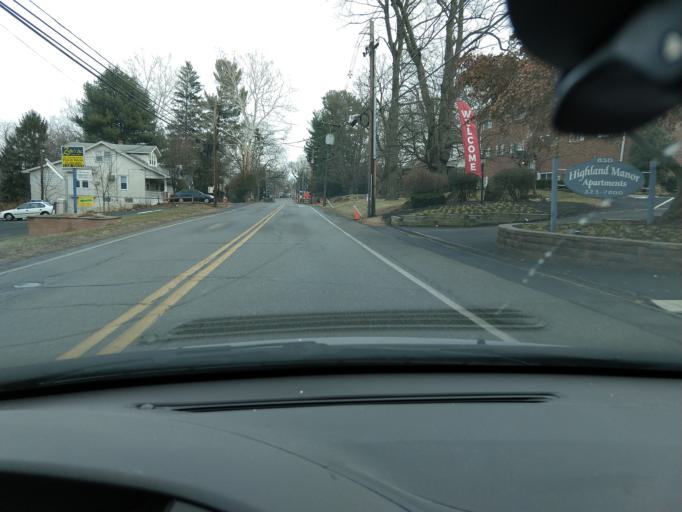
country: US
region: Pennsylvania
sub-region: Chester County
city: Kenilworth
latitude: 40.2323
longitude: -75.6391
